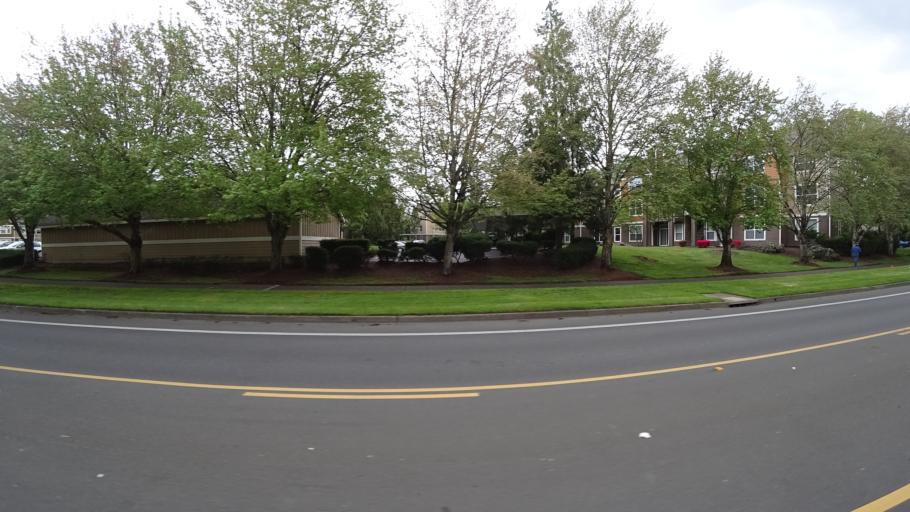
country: US
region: Oregon
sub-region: Washington County
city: Rockcreek
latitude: 45.5406
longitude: -122.8859
